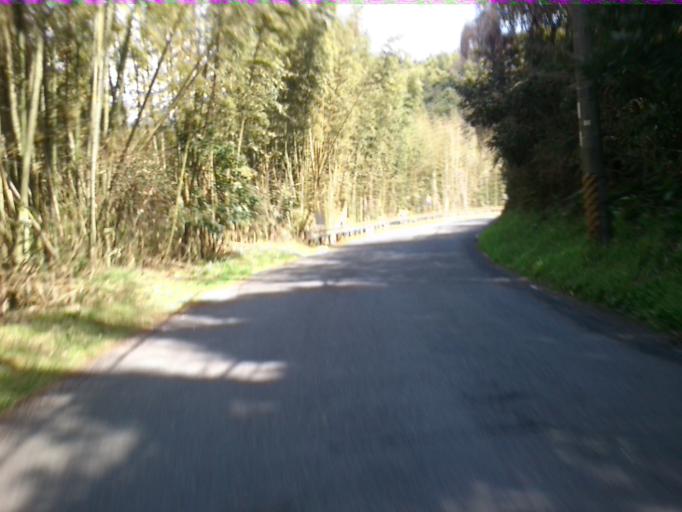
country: JP
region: Nara
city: Nara-shi
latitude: 34.7397
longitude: 135.8816
